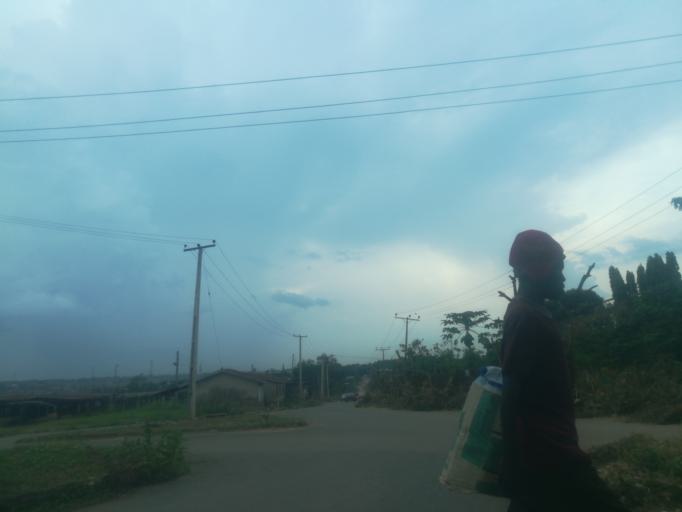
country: NG
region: Oyo
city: Ibadan
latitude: 7.4324
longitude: 3.9023
